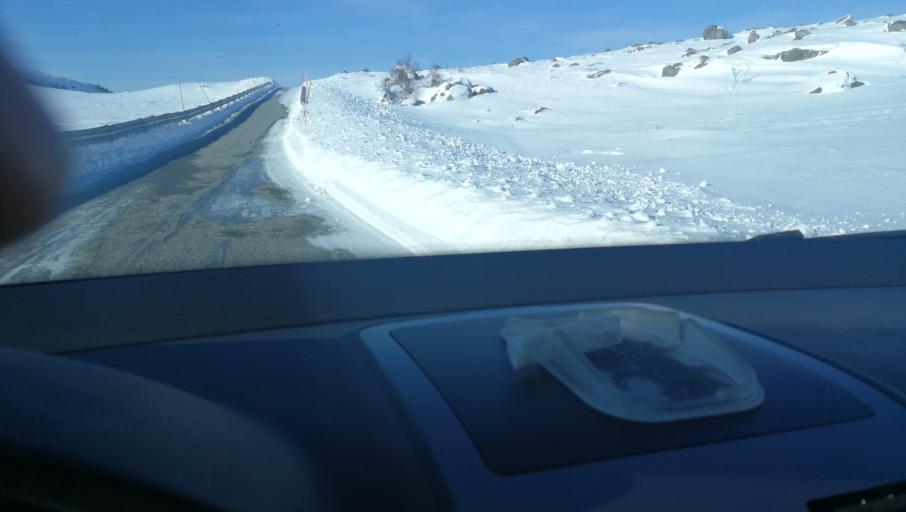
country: NO
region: Rogaland
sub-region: Hjelmeland
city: Hjelmelandsvagen
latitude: 59.0994
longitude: 6.3901
